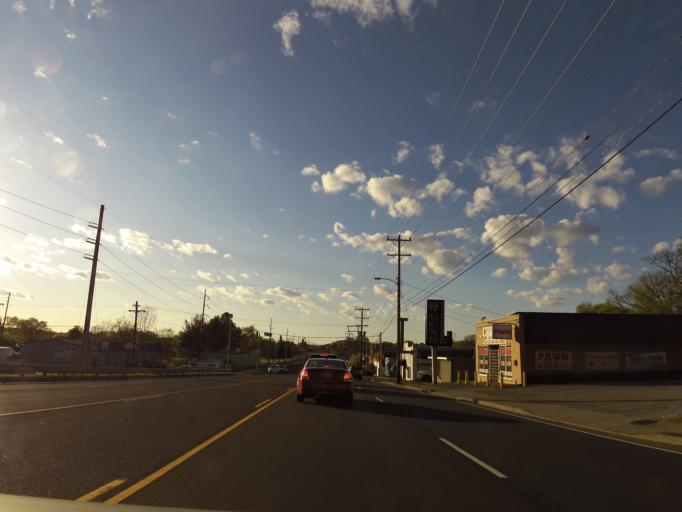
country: US
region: Tennessee
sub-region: Davidson County
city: Lakewood
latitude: 36.2470
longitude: -86.6405
